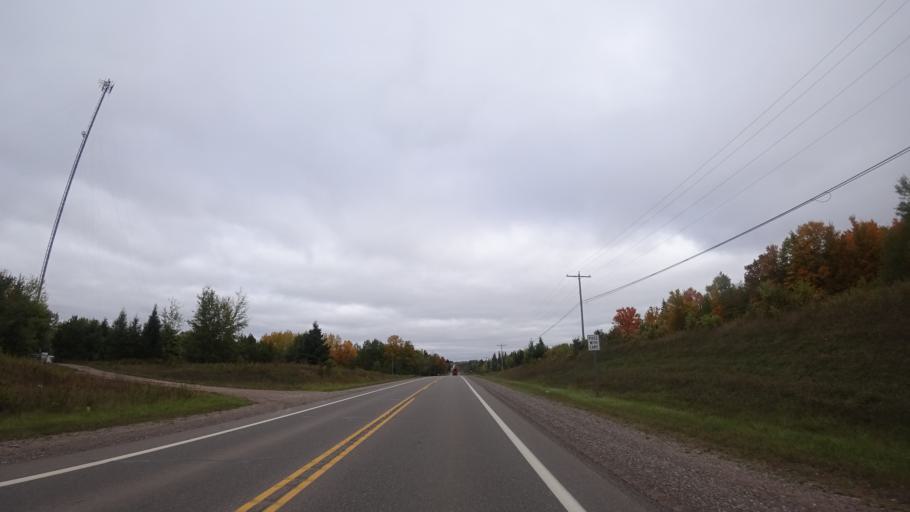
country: US
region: Wisconsin
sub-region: Florence County
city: Florence
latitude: 46.0934
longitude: -88.0757
